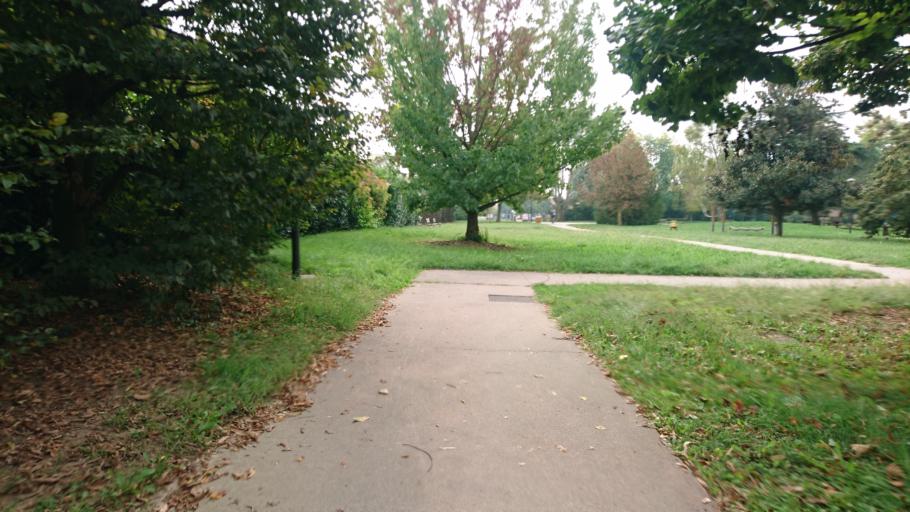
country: IT
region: Veneto
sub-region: Provincia di Padova
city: Tencarola
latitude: 45.3978
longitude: 11.8096
